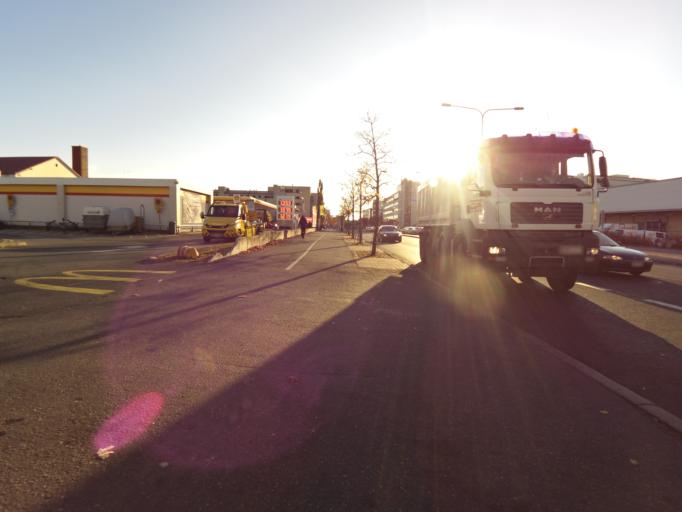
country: FI
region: Uusimaa
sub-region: Helsinki
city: Vantaa
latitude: 60.1942
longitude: 25.0372
